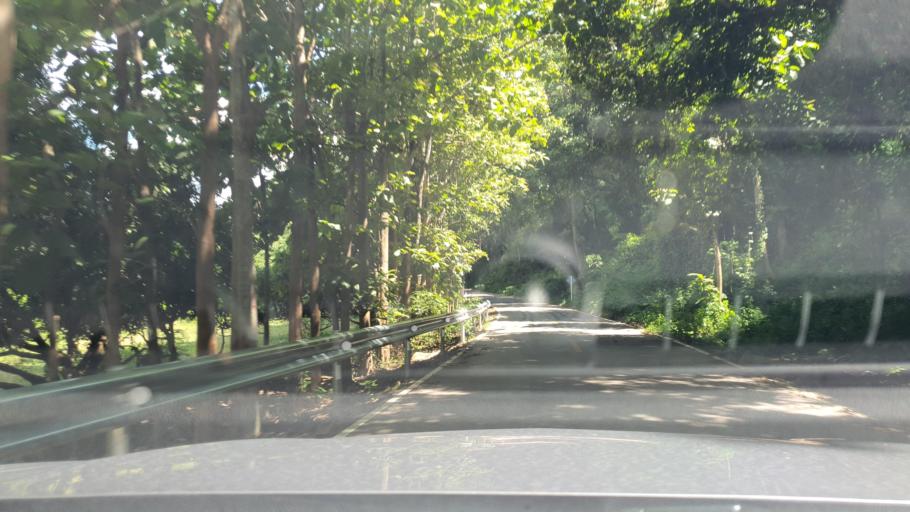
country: TH
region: Chiang Mai
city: Mae On
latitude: 18.7188
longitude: 99.2305
